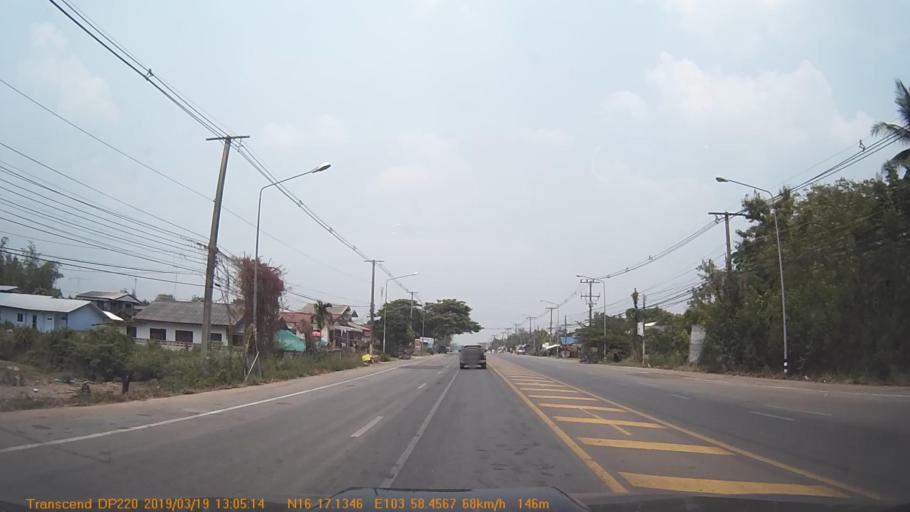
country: TH
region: Roi Et
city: Waeng
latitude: 16.2858
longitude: 103.9743
